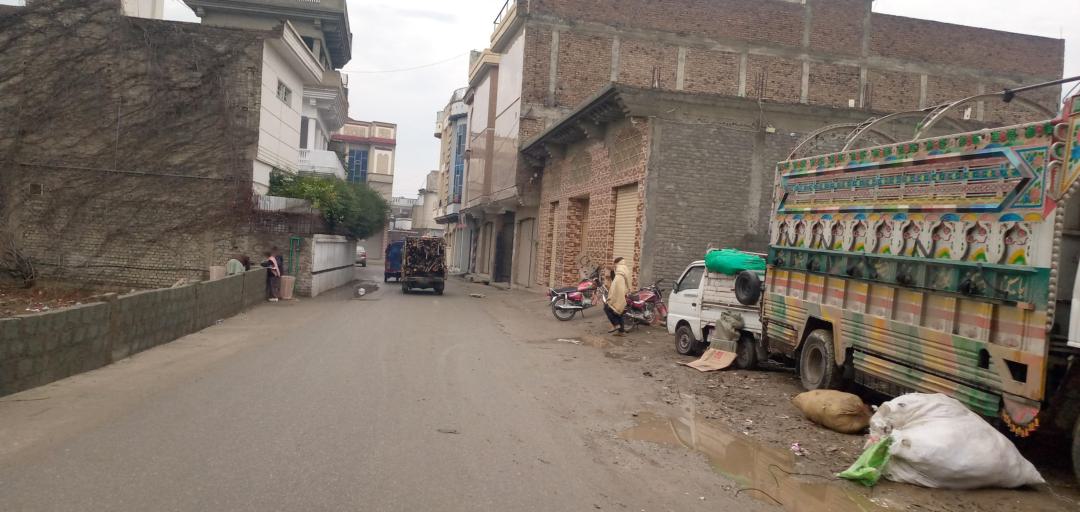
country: PK
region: Khyber Pakhtunkhwa
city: Mingora
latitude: 34.7797
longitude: 72.3548
